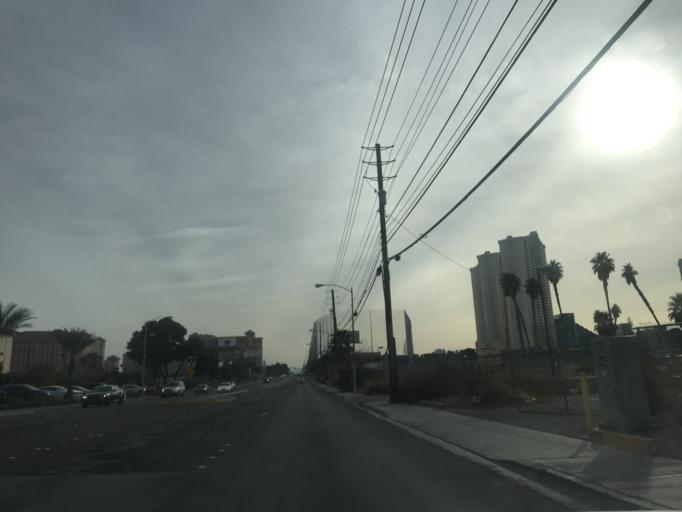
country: US
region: Nevada
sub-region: Clark County
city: Paradise
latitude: 36.1126
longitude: -115.1641
